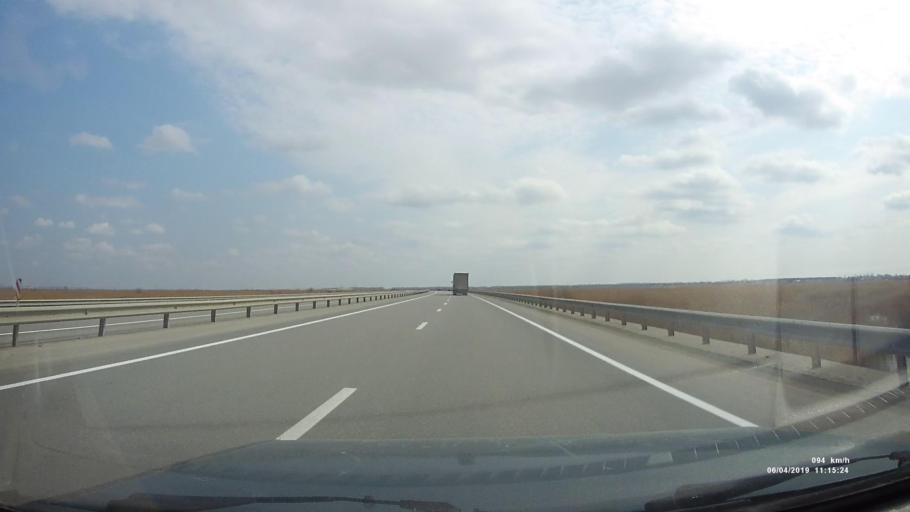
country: RU
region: Rostov
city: Kuleshovka
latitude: 47.0887
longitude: 39.5428
